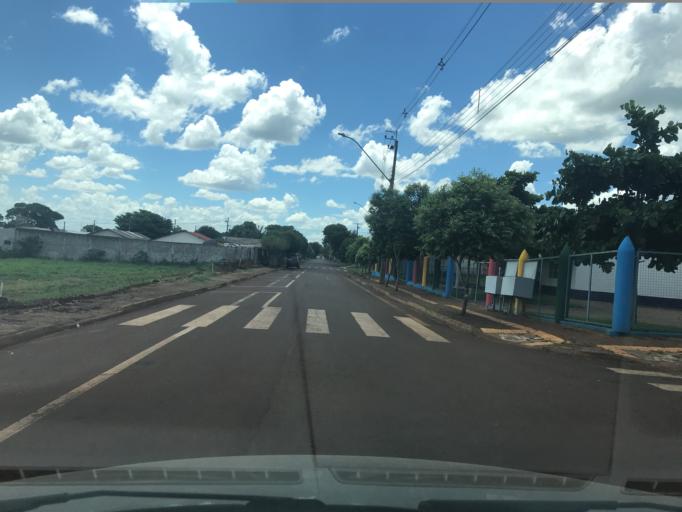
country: BR
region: Parana
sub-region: Palotina
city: Palotina
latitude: -24.2735
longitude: -53.8476
